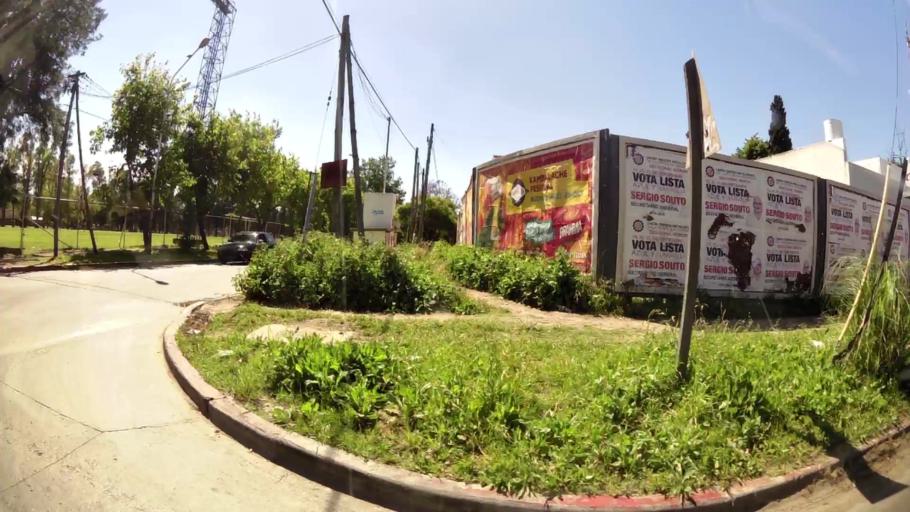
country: AR
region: Buenos Aires
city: Ituzaingo
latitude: -34.6608
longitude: -58.6610
